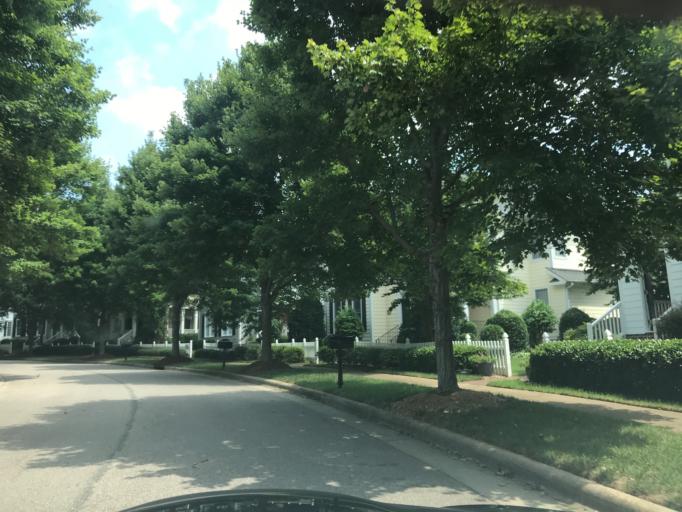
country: US
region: North Carolina
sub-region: Wake County
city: Wake Forest
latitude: 35.9272
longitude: -78.5724
